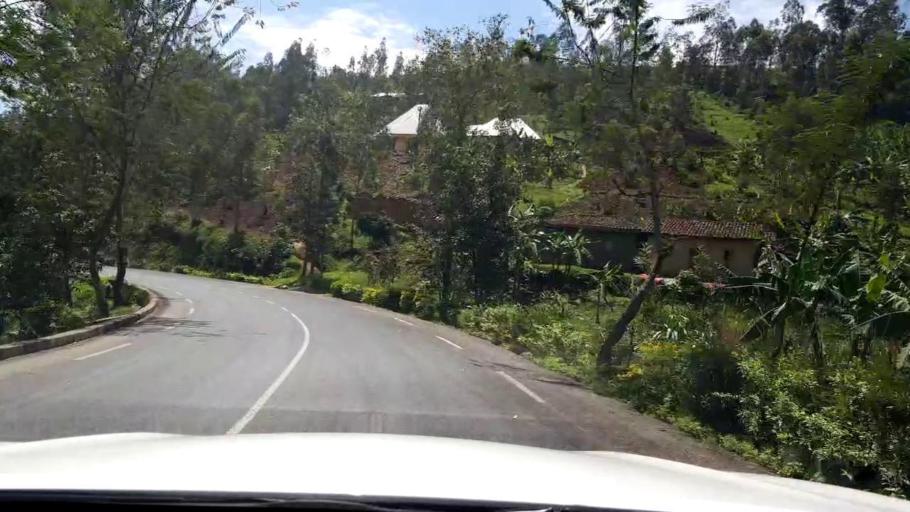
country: RW
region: Southern Province
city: Gitarama
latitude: -1.9214
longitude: 29.6494
